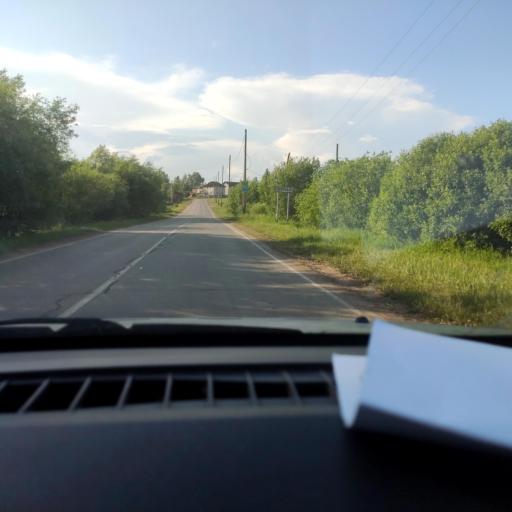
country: RU
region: Perm
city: Krasnokamsk
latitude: 58.1375
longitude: 55.7383
